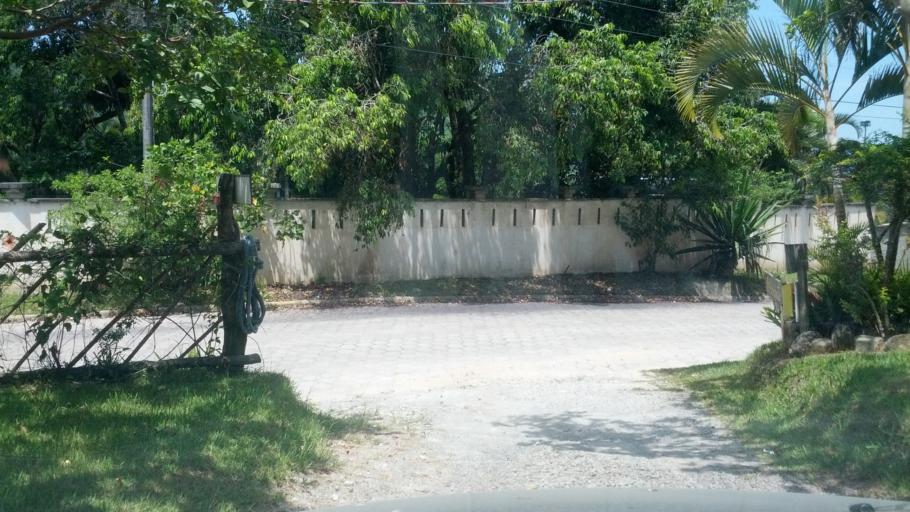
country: BR
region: Santa Catarina
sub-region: Porto Belo
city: Porto Belo
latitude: -27.1642
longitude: -48.5239
